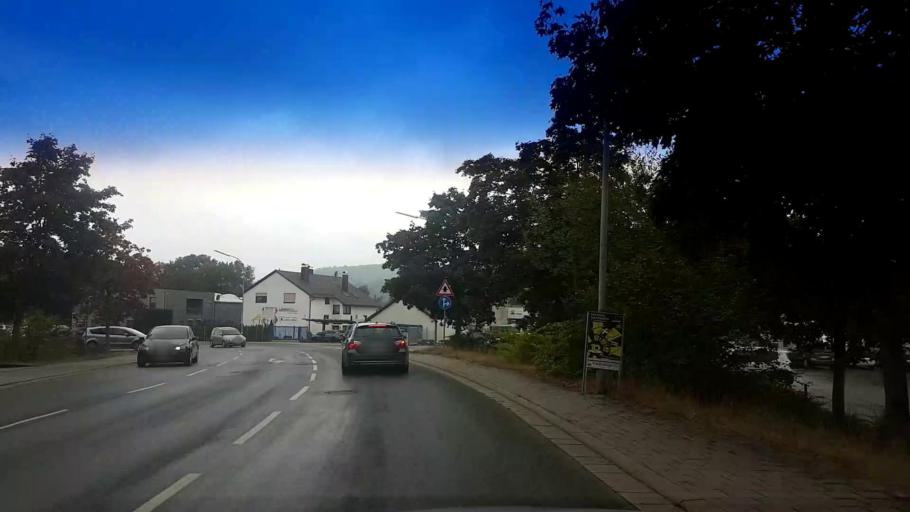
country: DE
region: Bavaria
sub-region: Upper Franconia
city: Forchheim
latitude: 49.7340
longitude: 11.0564
